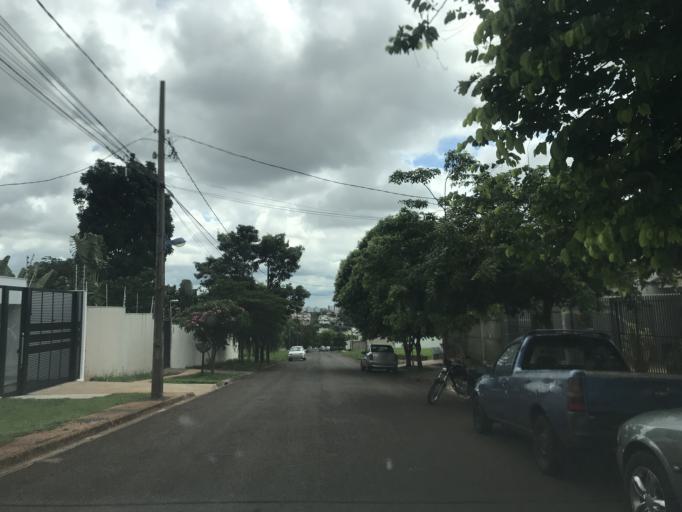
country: BR
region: Parana
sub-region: Maringa
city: Maringa
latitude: -23.4474
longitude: -51.9484
